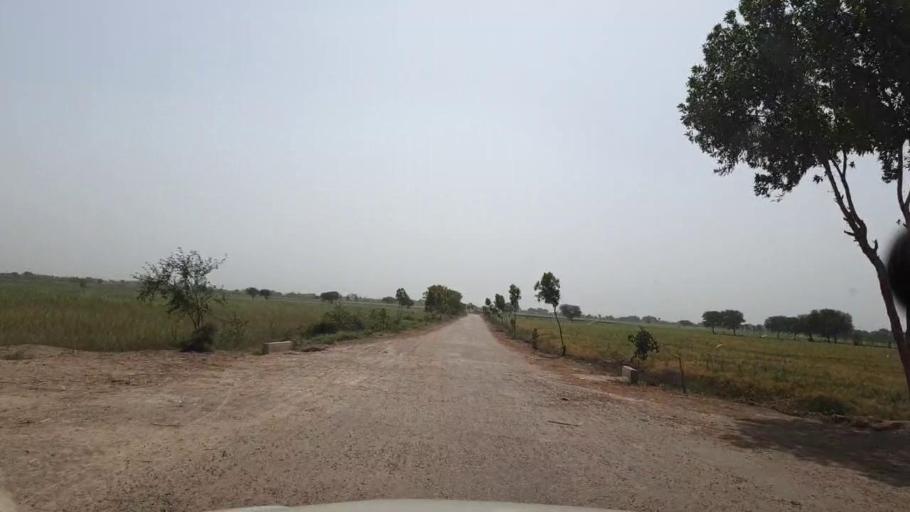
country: PK
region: Sindh
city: Matli
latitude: 25.0505
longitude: 68.6821
